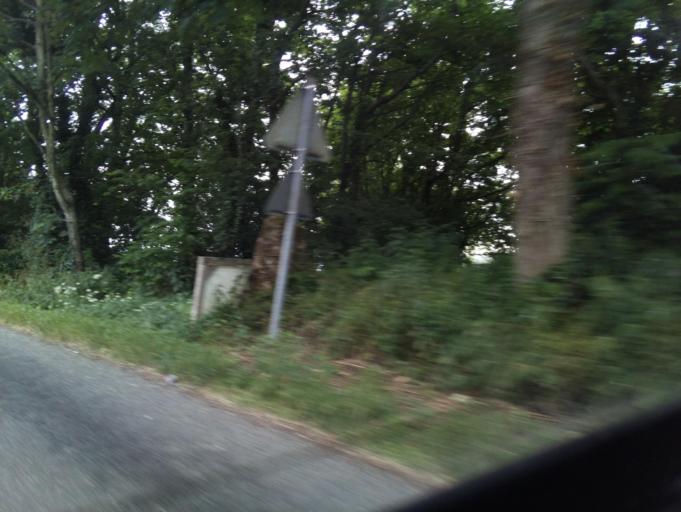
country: GB
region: England
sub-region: Somerset
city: Crewkerne
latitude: 50.8811
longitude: -2.7489
